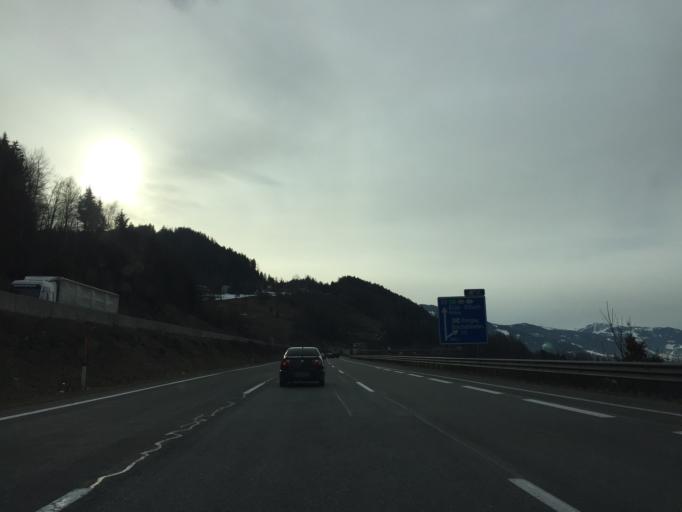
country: AT
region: Salzburg
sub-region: Politischer Bezirk Sankt Johann im Pongau
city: Pfarrwerfen
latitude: 47.4550
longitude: 13.2145
